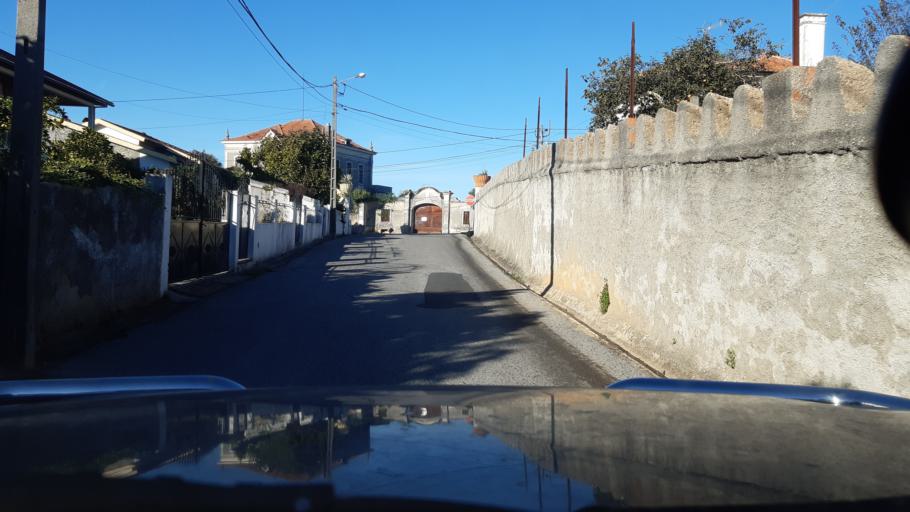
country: PT
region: Aveiro
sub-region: Agueda
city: Agueda
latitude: 40.5567
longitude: -8.4368
